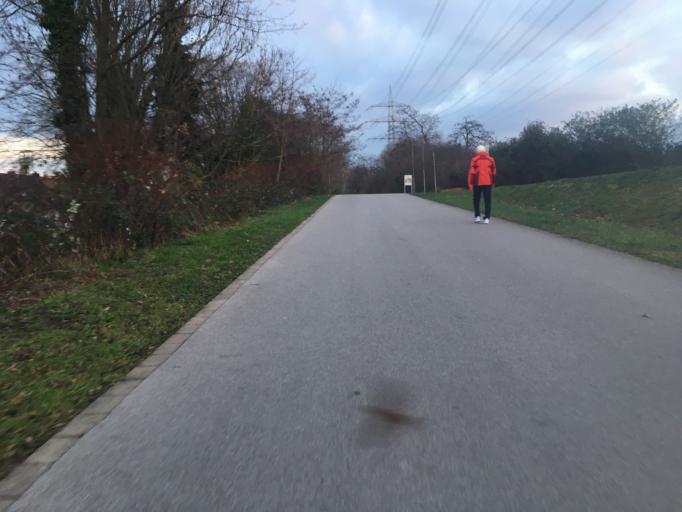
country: DE
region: North Rhine-Westphalia
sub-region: Regierungsbezirk Dusseldorf
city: Essen
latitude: 51.4662
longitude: 6.9784
